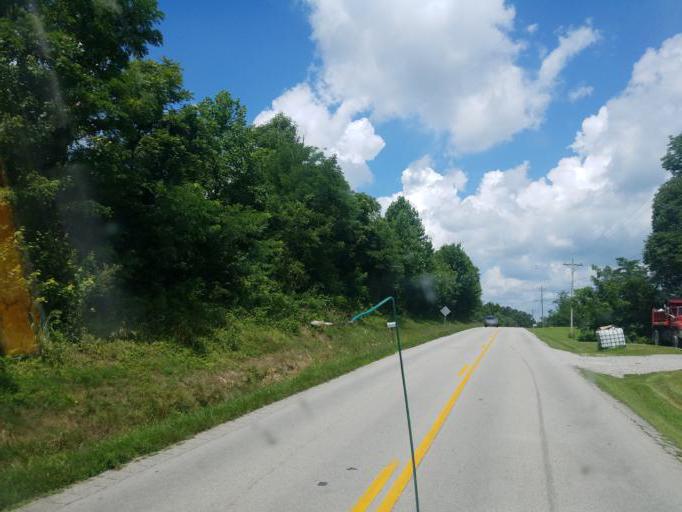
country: US
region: Kentucky
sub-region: Grayson County
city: Leitchfield
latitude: 37.4943
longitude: -86.3020
